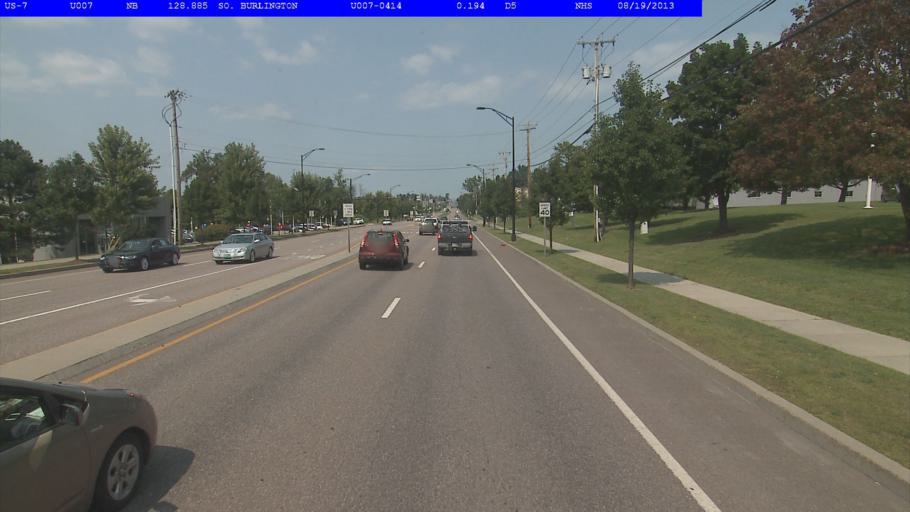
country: US
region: Vermont
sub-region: Chittenden County
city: Burlington
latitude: 44.4229
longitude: -73.2118
